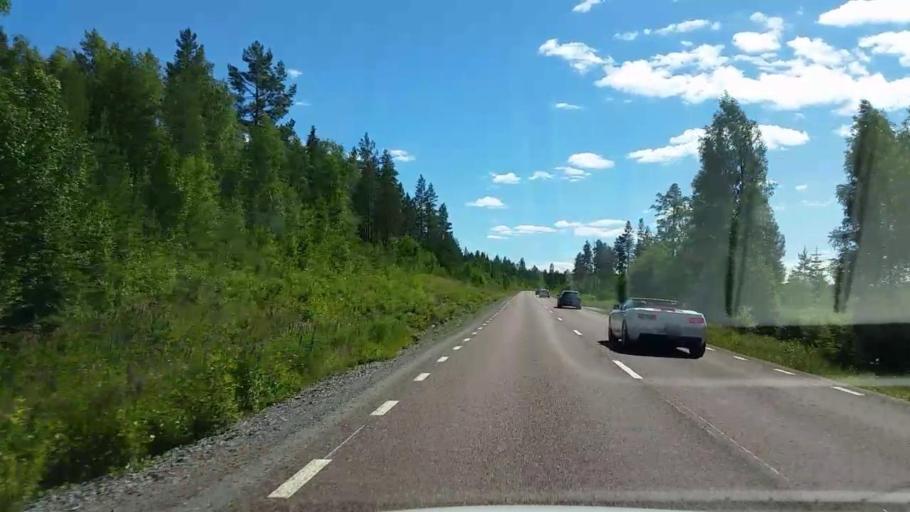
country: SE
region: Gaevleborg
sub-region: Ovanakers Kommun
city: Edsbyn
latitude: 61.2212
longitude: 15.8769
